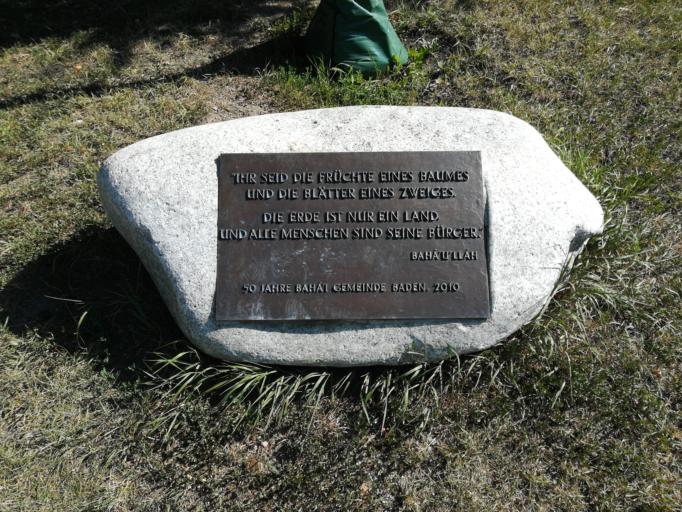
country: AT
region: Lower Austria
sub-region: Politischer Bezirk Baden
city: Baden
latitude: 48.0129
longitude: 16.2335
